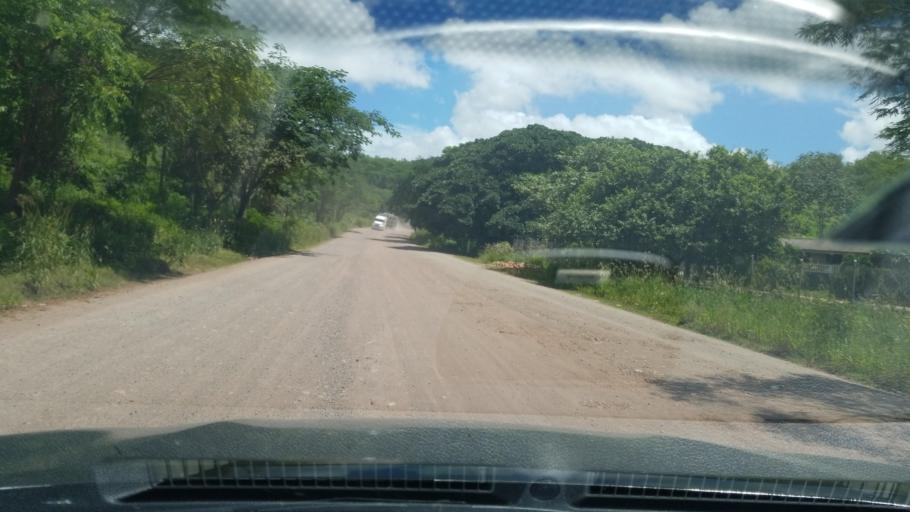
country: HN
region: Francisco Morazan
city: San Juan de Flores
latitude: 14.3212
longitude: -87.0460
